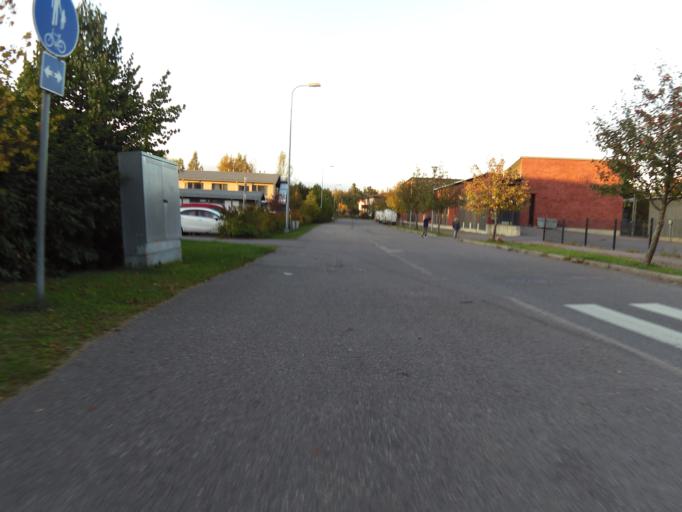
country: FI
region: Uusimaa
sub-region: Helsinki
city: Kilo
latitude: 60.2757
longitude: 24.7509
